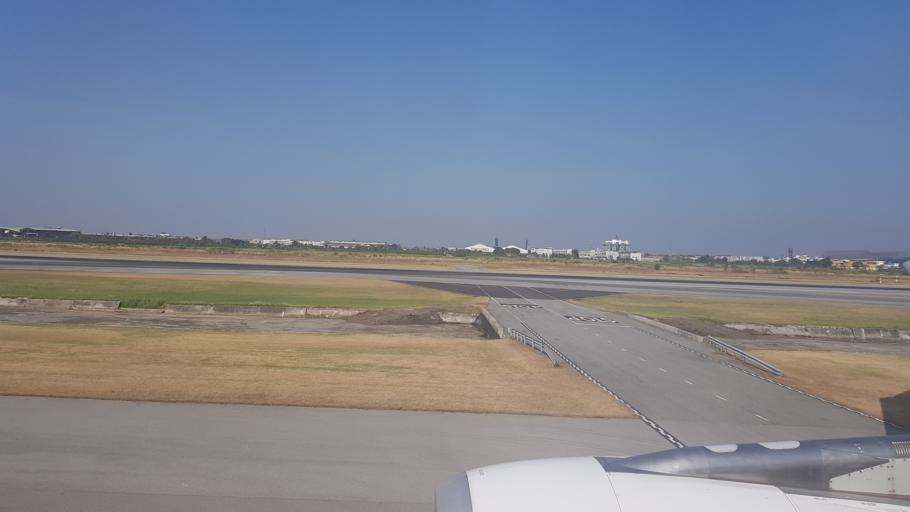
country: TH
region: Bangkok
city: Lat Krabang
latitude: 13.6843
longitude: 100.7400
